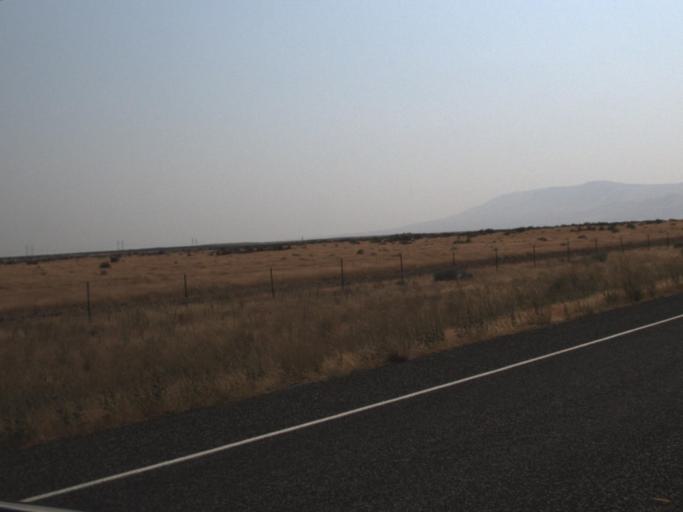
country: US
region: Washington
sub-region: Grant County
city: Desert Aire
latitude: 46.5892
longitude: -119.7277
